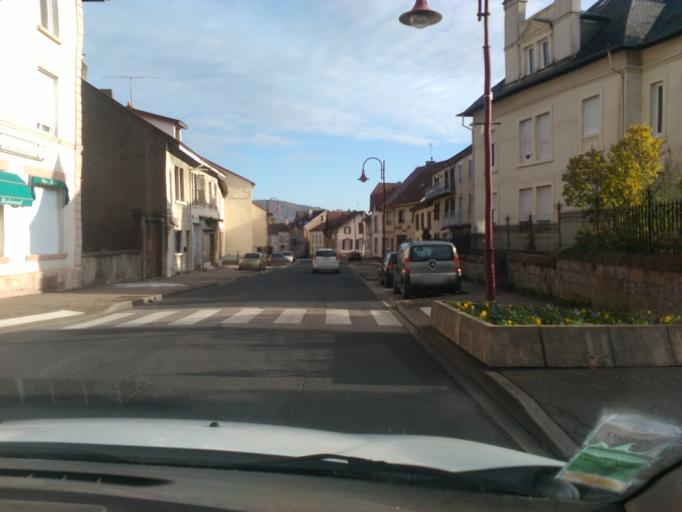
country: FR
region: Lorraine
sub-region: Departement des Vosges
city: Etival-Clairefontaine
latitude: 48.4038
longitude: 6.8385
